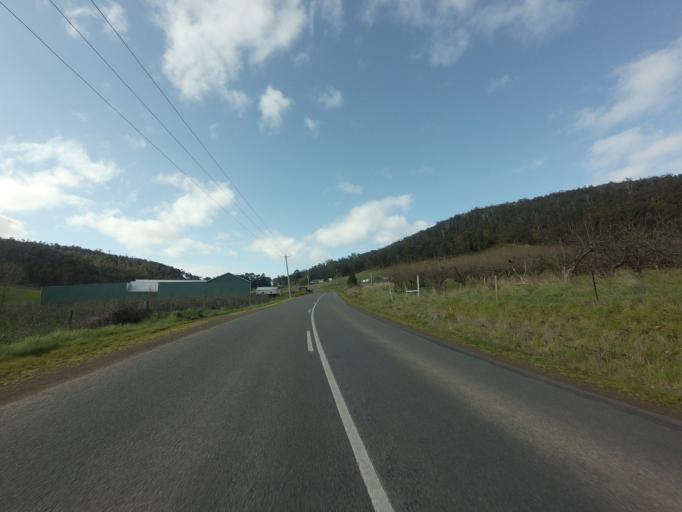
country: AU
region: Tasmania
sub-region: Huon Valley
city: Geeveston
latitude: -43.1725
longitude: 146.9448
